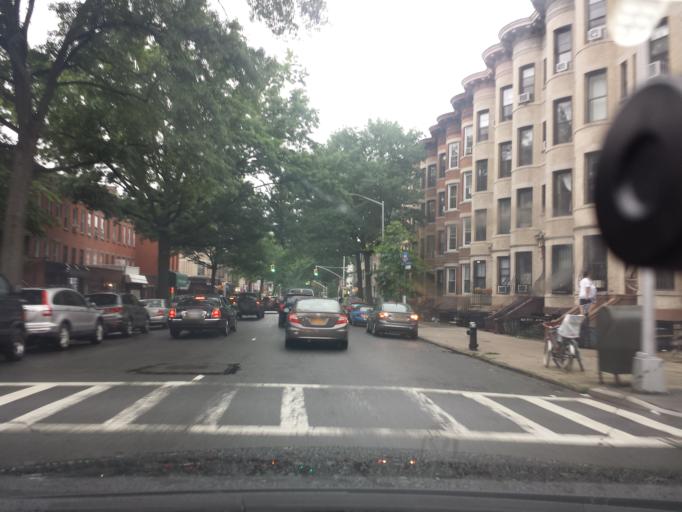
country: US
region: New York
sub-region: Kings County
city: Brooklyn
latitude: 40.6634
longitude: -73.9813
